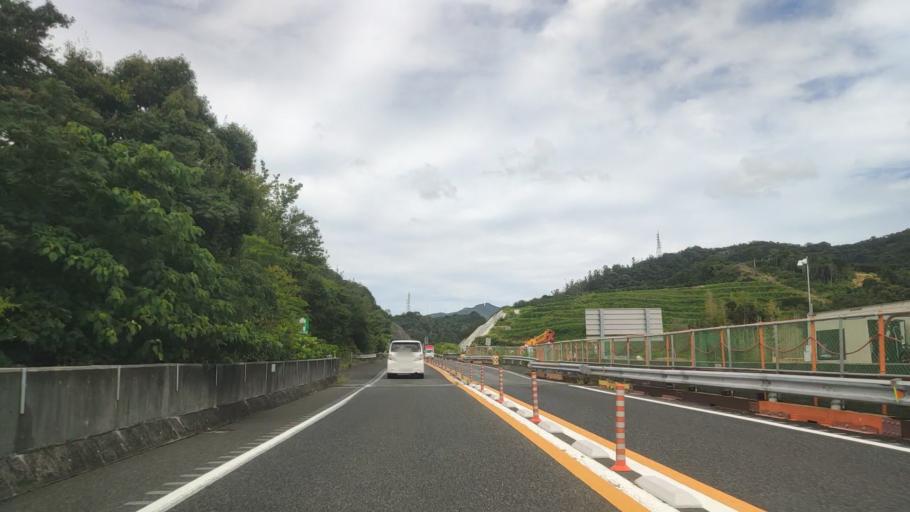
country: JP
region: Wakayama
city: Gobo
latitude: 33.9157
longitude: 135.1941
